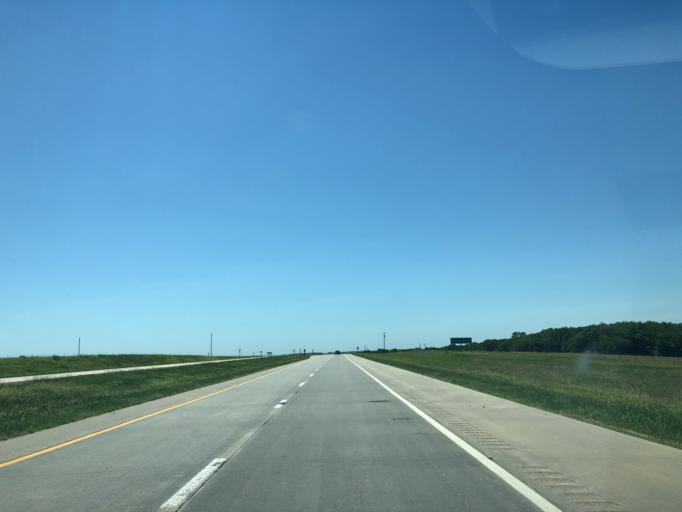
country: US
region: Kansas
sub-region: Cloud County
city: Concordia
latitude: 39.6266
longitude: -97.6604
